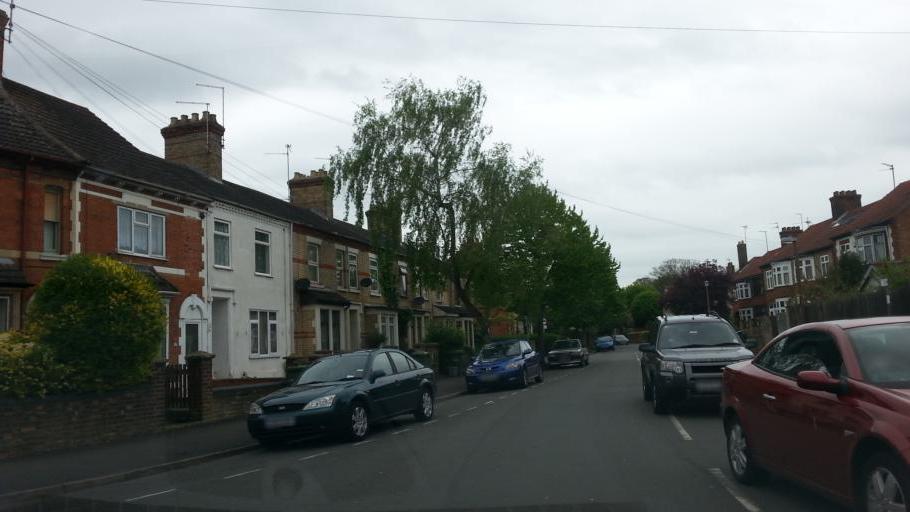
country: GB
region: England
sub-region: Peterborough
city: Peterborough
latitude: 52.5812
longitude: -0.2324
